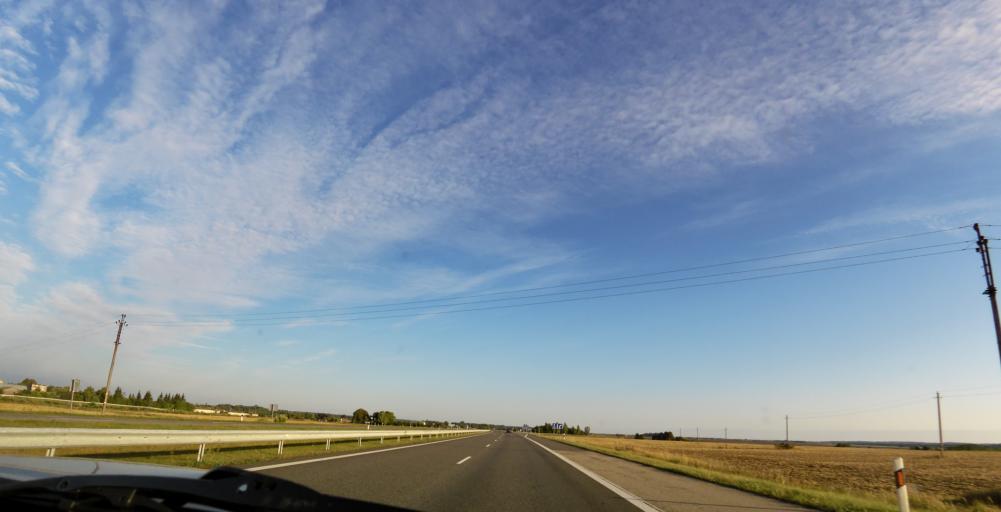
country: LT
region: Vilnius County
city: Ukmerge
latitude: 55.2976
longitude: 24.7976
